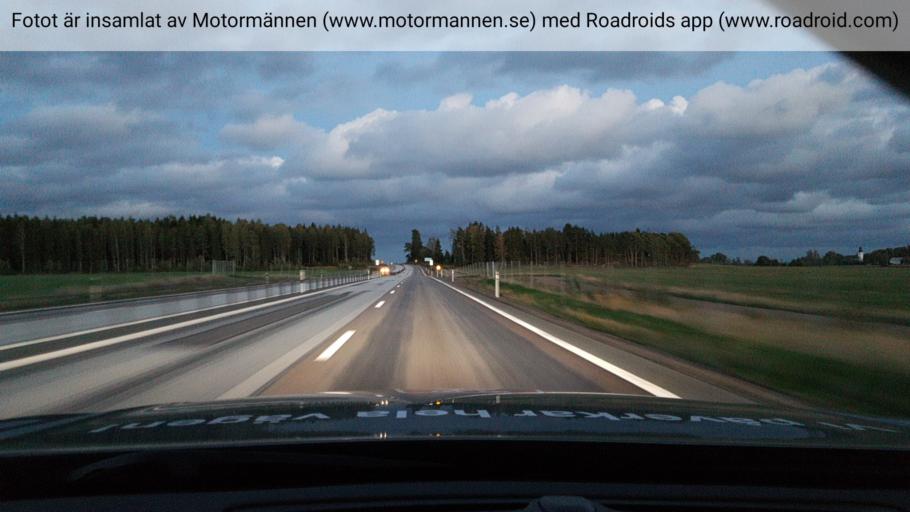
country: SE
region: Vaermland
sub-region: Kristinehamns Kommun
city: Kristinehamn
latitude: 59.3776
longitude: 13.9191
